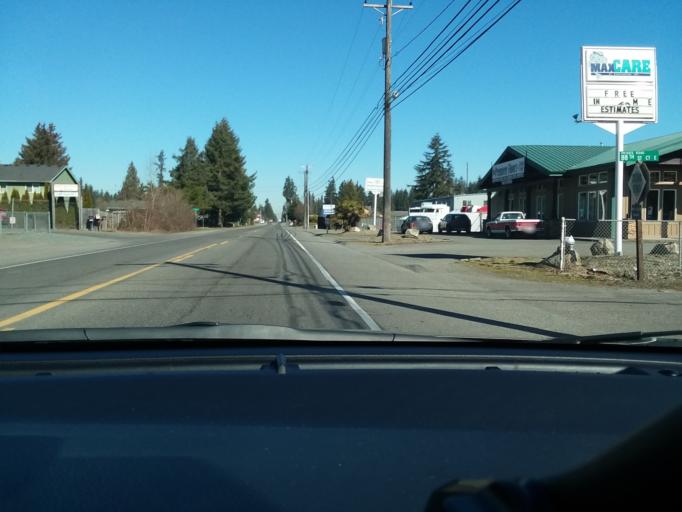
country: US
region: Washington
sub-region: Pierce County
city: Summit
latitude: 47.1769
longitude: -122.3571
